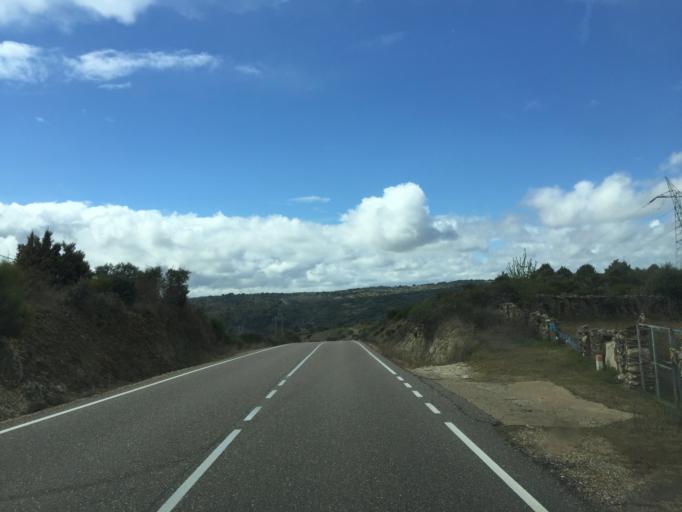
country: ES
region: Castille and Leon
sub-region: Provincia de Zamora
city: Moral de Sayago
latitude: 41.4989
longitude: -6.0800
